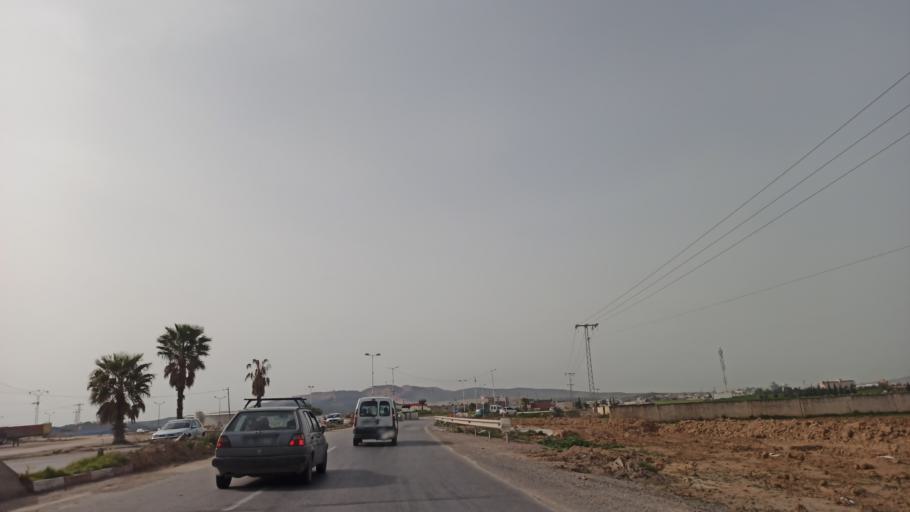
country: TN
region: Tunis
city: La Mohammedia
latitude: 36.5658
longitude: 10.0832
